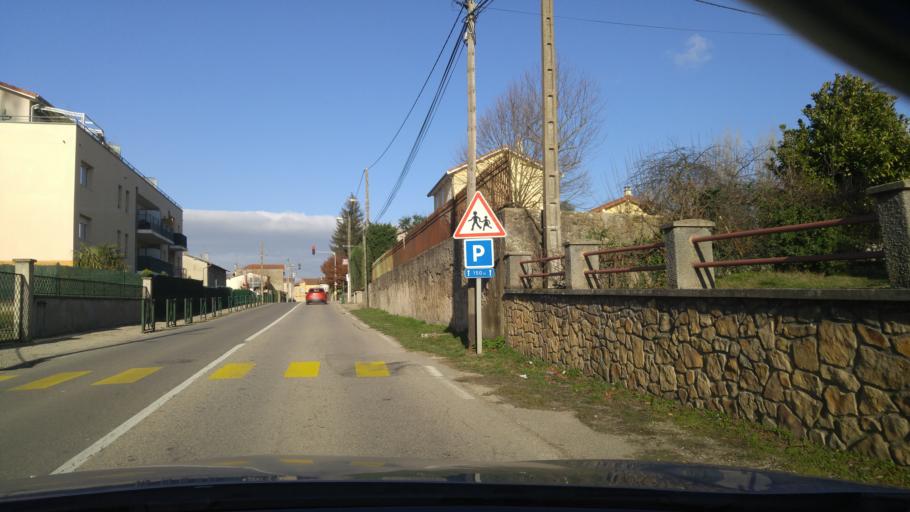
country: FR
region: Rhone-Alpes
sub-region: Departement de l'Isere
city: Tignieu-Jameyzieu
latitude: 45.7327
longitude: 5.1870
